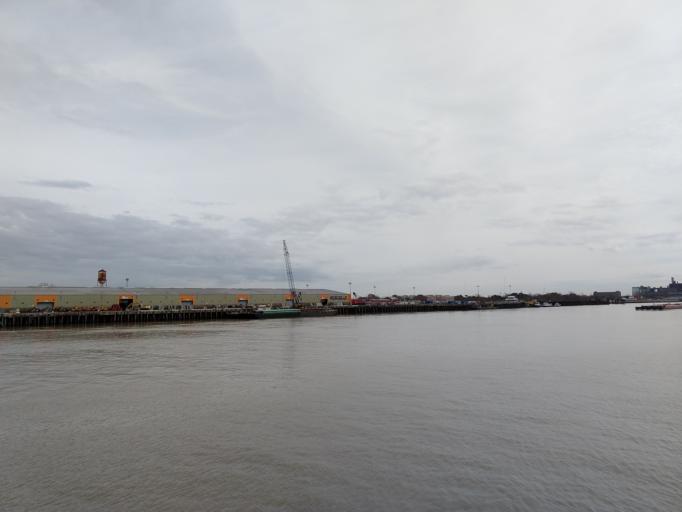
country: US
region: Louisiana
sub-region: Saint Bernard Parish
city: Arabi
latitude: 29.9515
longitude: -90.0208
